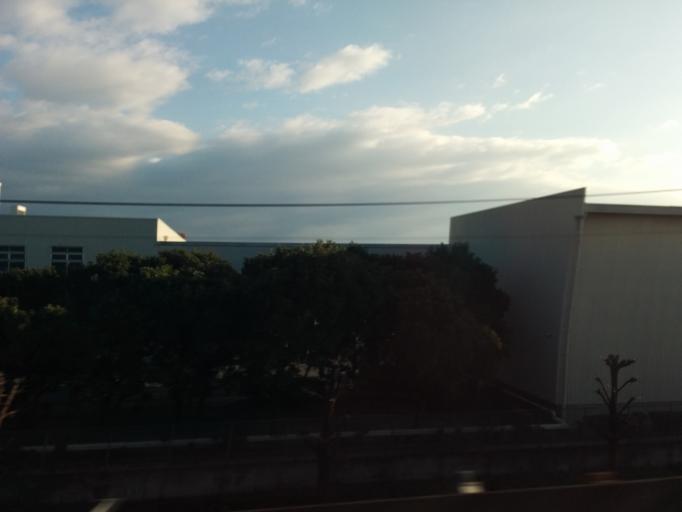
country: JP
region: Aichi
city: Anjo
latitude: 34.9748
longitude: 137.0551
